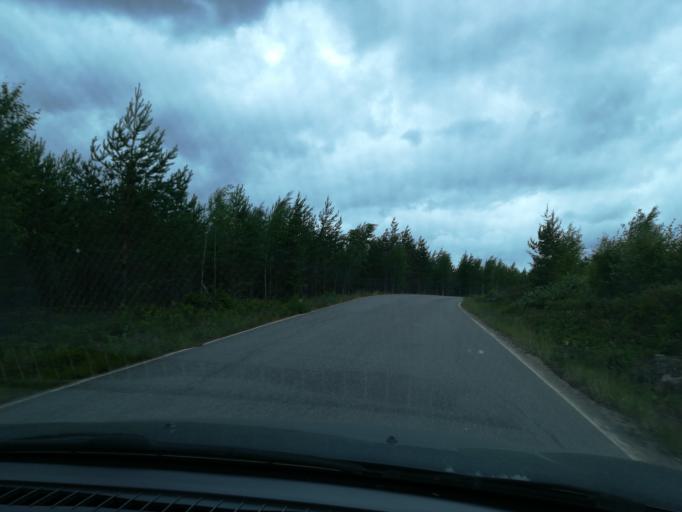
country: FI
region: South Karelia
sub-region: Lappeenranta
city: Savitaipale
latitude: 61.3219
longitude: 27.4859
